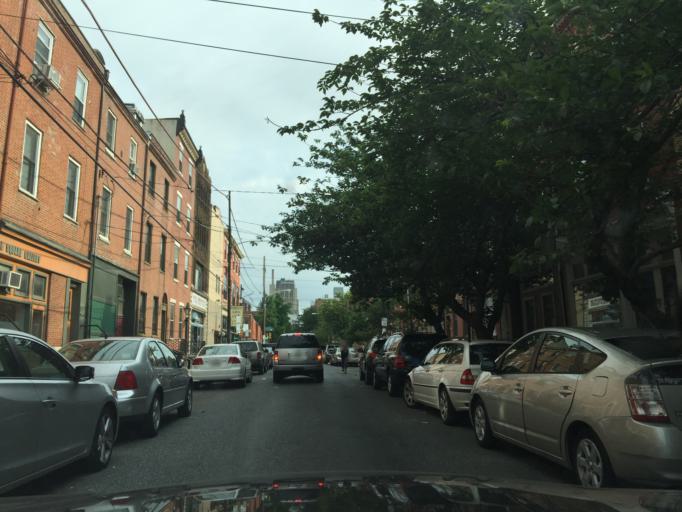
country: US
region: Pennsylvania
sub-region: Philadelphia County
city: Philadelphia
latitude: 39.9419
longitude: -75.1572
